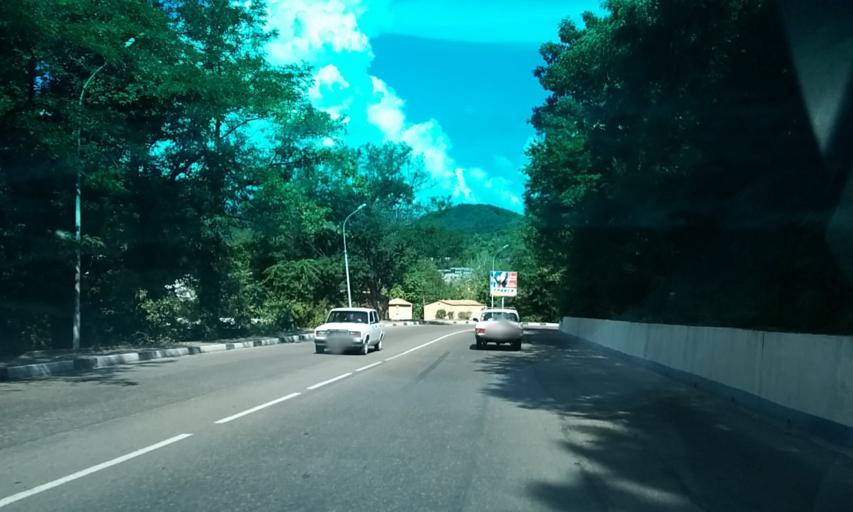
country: RU
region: Krasnodarskiy
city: Tuapse
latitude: 44.1064
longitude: 39.0629
